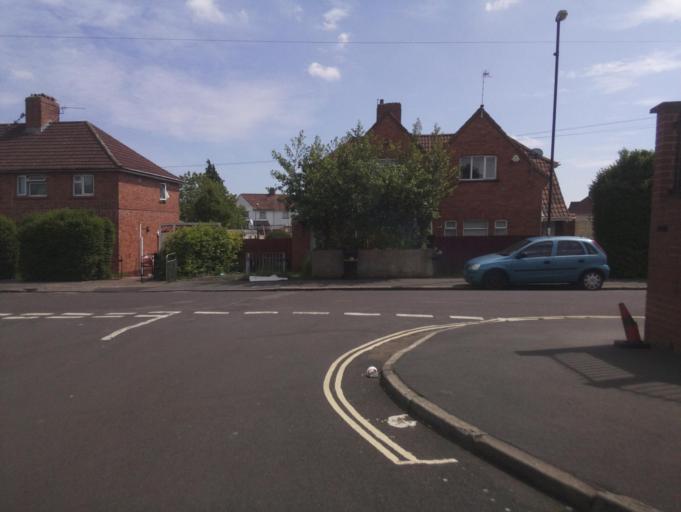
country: GB
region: England
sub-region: Bristol
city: Bristol
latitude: 51.5022
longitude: -2.5965
